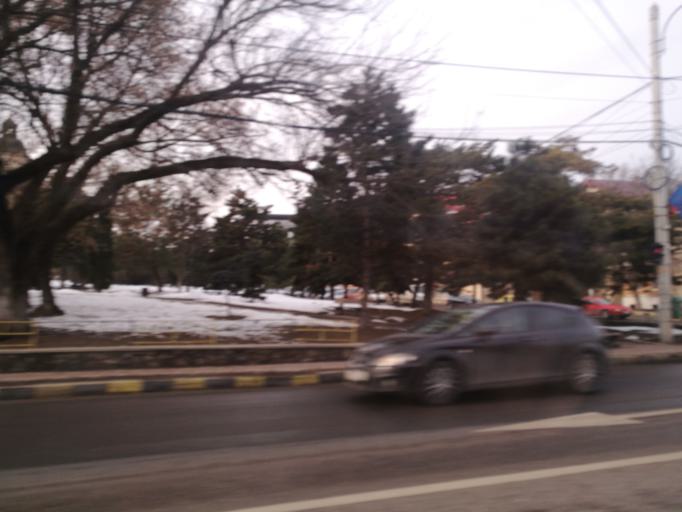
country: RO
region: Suceava
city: Suceava
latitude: 47.6459
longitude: 26.2639
